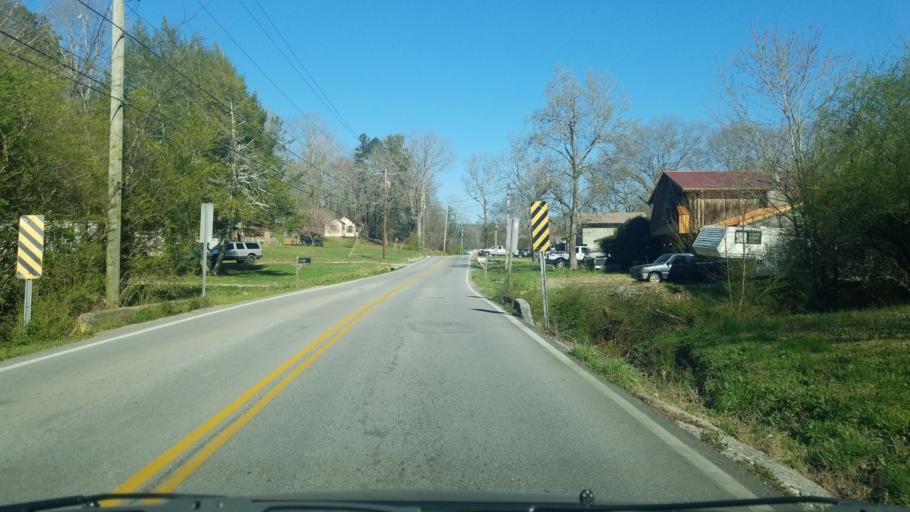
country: US
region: Tennessee
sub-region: Hamilton County
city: Middle Valley
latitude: 35.2111
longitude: -85.1739
